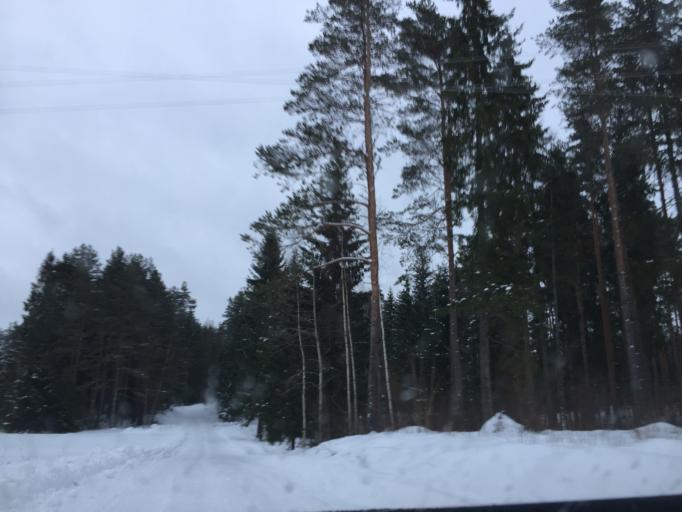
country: LV
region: Amatas Novads
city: Drabesi
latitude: 57.2058
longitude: 25.3002
